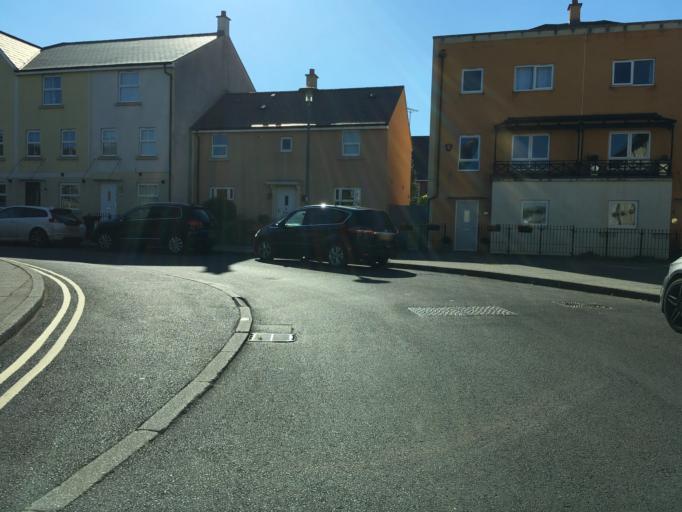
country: GB
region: England
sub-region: North Somerset
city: Portishead
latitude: 51.4879
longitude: -2.7533
